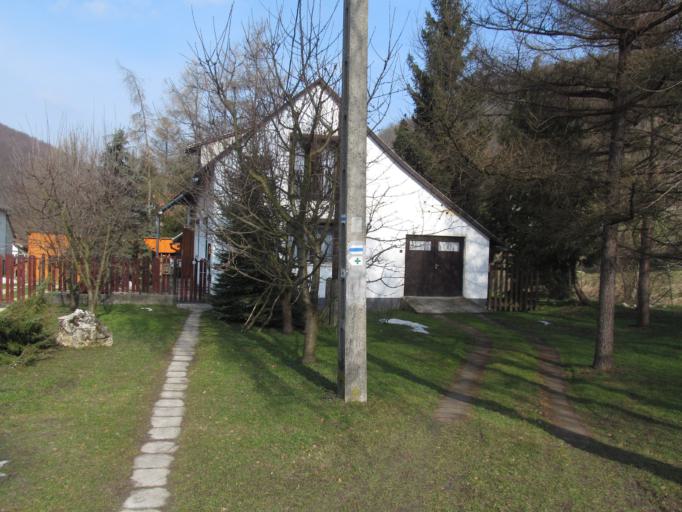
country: HU
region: Veszprem
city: Herend
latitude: 47.2581
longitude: 17.7205
